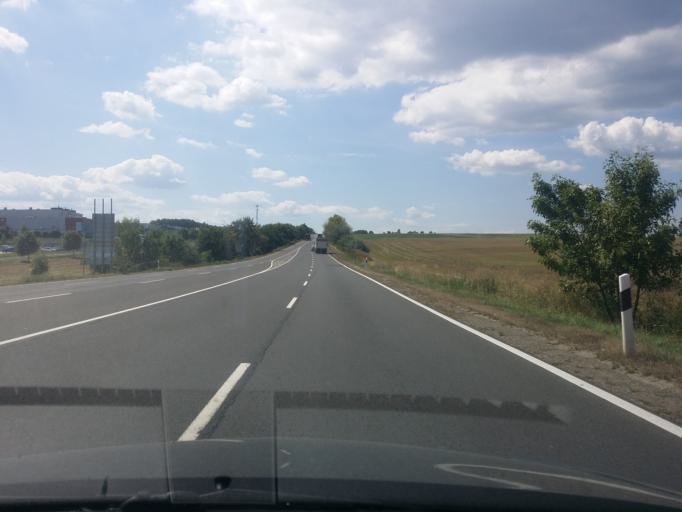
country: HU
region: Nograd
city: Retsag
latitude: 47.9178
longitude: 19.1179
